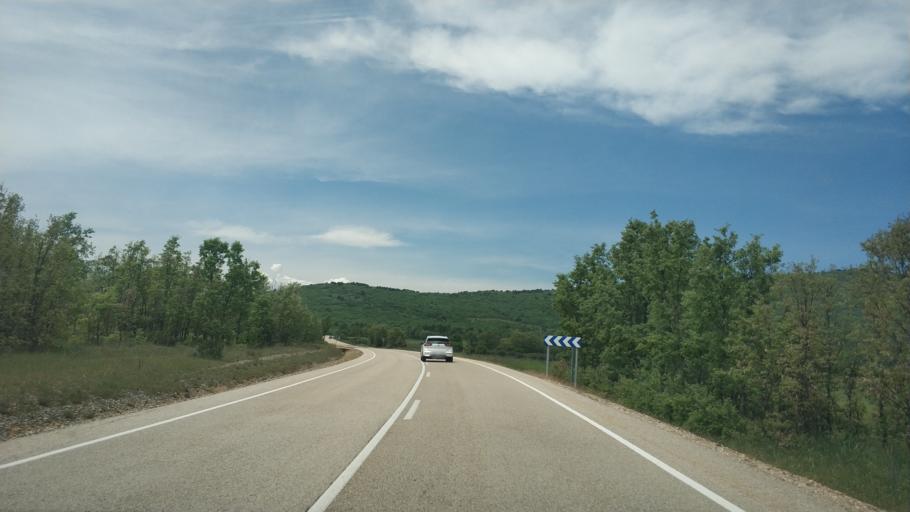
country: ES
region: Castille and Leon
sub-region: Provincia de Soria
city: Vinuesa
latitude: 41.8878
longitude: -2.6911
